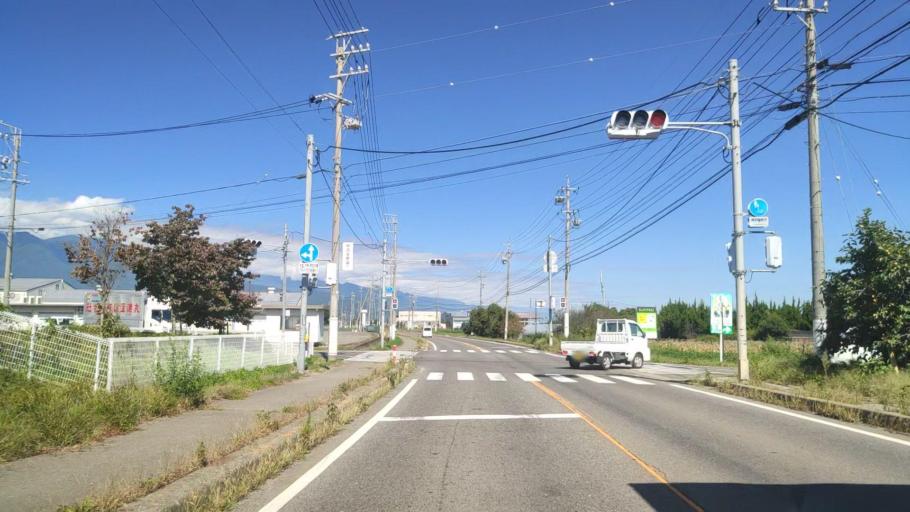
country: JP
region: Nagano
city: Matsumoto
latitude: 36.2009
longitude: 137.9022
